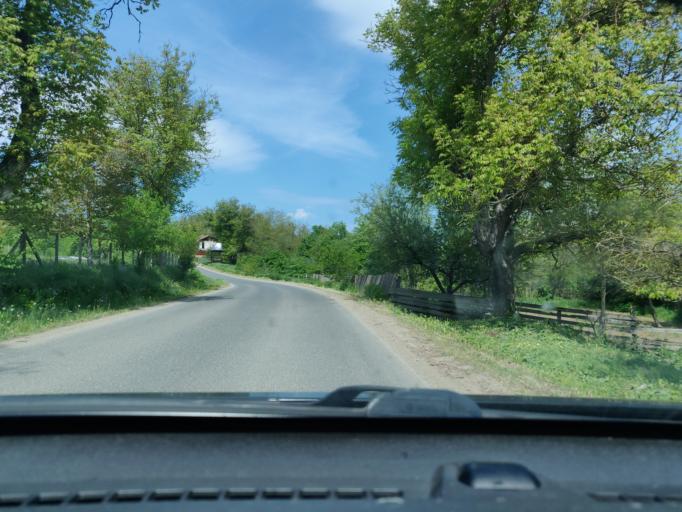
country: RO
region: Vrancea
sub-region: Comuna Vidra
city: Vidra
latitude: 45.9518
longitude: 26.8619
